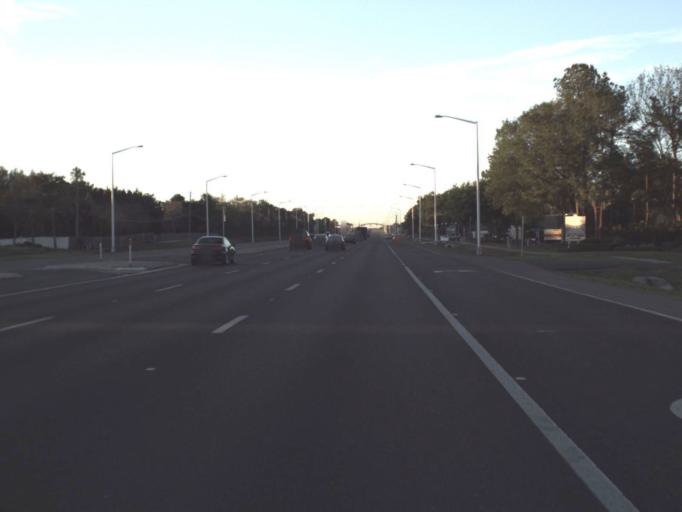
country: US
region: Florida
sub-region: Orange County
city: Union Park
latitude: 28.5850
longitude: -81.3068
